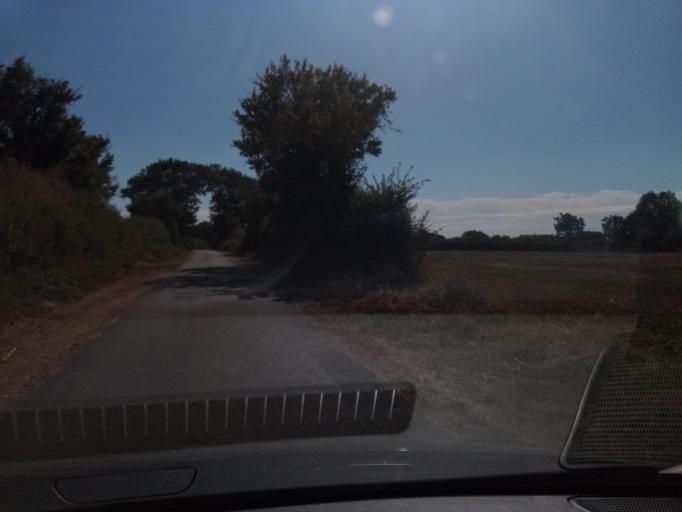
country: FR
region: Poitou-Charentes
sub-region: Departement de la Vienne
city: Lussac-les-Chateaux
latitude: 46.3968
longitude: 0.7518
